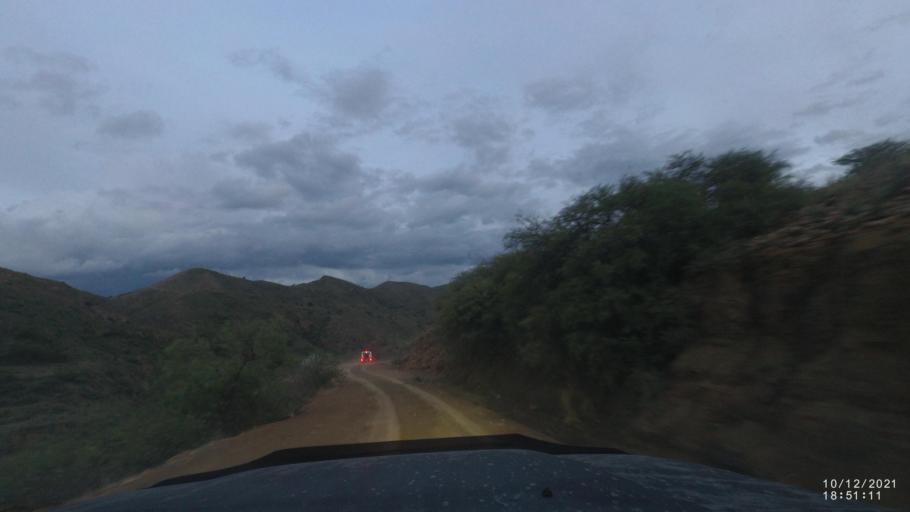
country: BO
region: Cochabamba
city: Tarata
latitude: -17.8813
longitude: -65.9669
